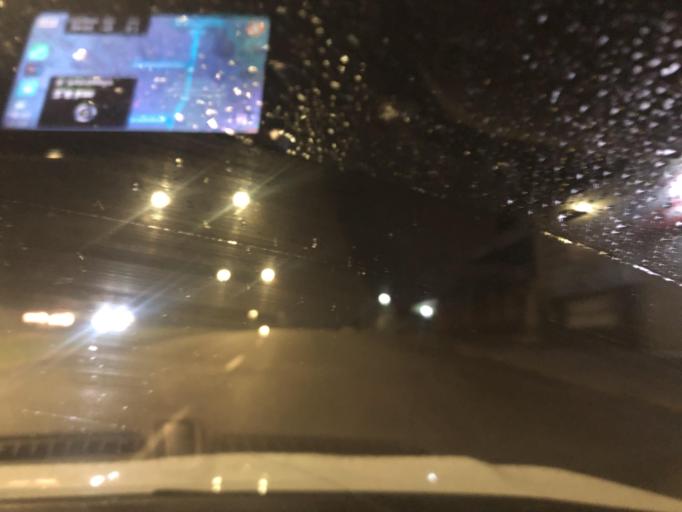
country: BR
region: Santa Catarina
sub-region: Joinville
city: Joinville
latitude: -26.3662
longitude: -48.8324
